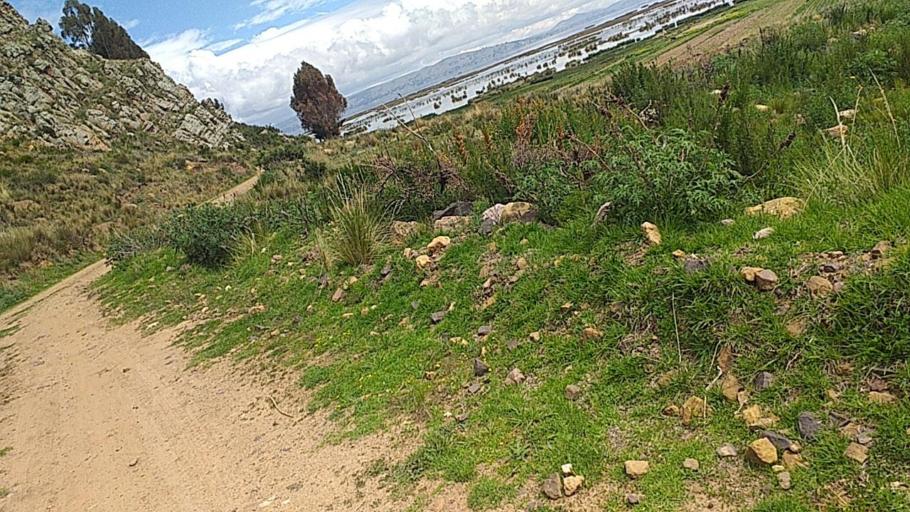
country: BO
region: La Paz
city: Batallas
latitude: -16.3289
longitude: -68.6424
